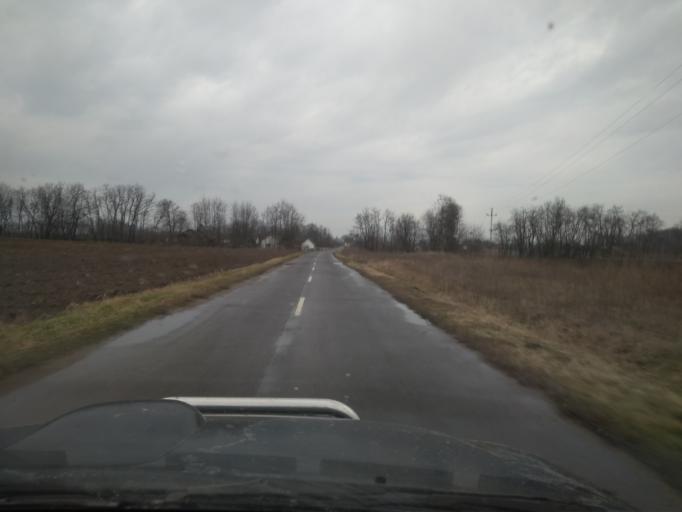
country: HU
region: Szabolcs-Szatmar-Bereg
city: Nyirtelek
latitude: 47.9665
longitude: 21.6475
